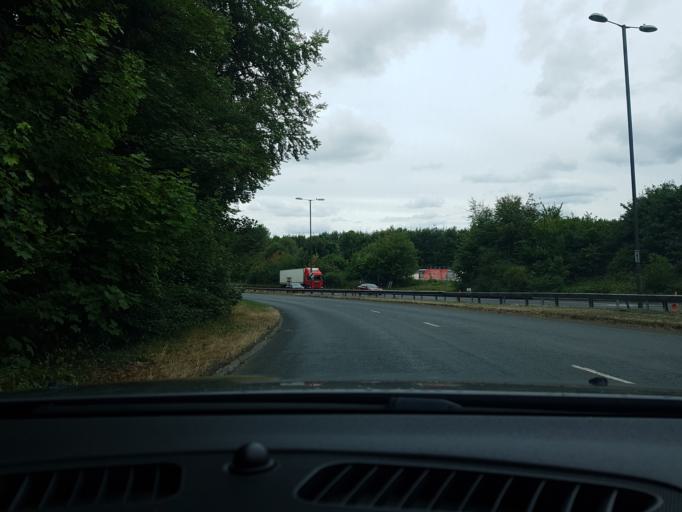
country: GB
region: England
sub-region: Hampshire
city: Basingstoke
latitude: 51.2753
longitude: -1.1130
